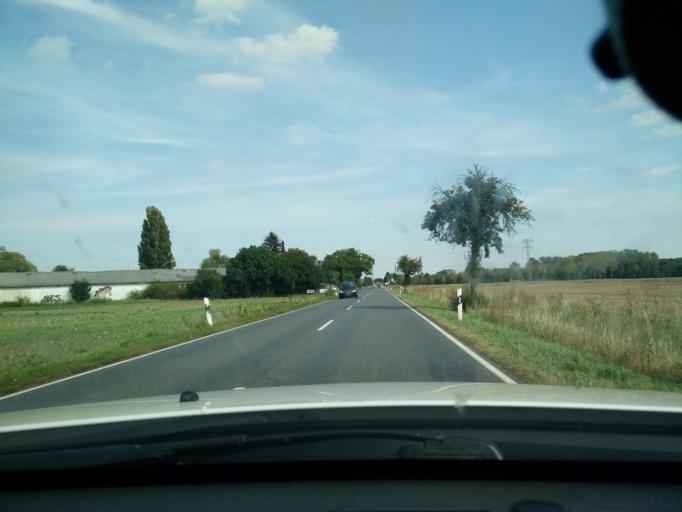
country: DE
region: Saxony-Anhalt
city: Schermen
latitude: 52.2770
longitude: 11.8063
